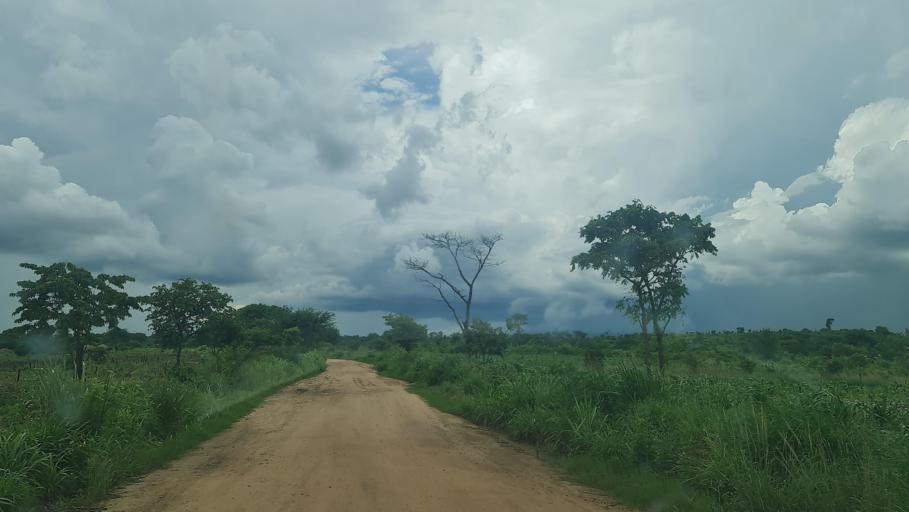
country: MW
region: Southern Region
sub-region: Nsanje District
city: Nsanje
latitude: -17.5703
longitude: 35.6518
